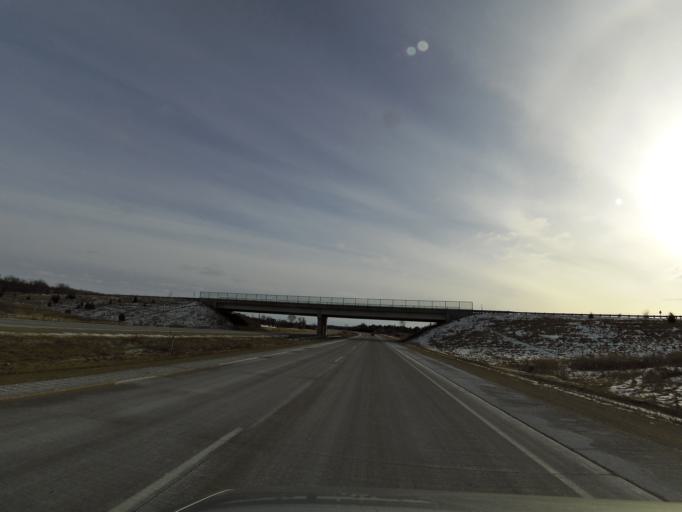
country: US
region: Wisconsin
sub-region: Saint Croix County
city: Hudson
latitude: 44.9432
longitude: -92.6942
